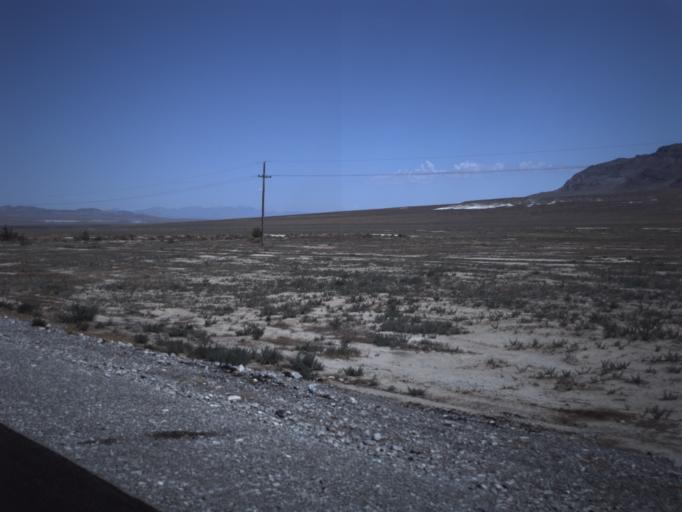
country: US
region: Utah
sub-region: Beaver County
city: Milford
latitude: 39.0591
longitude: -113.4355
